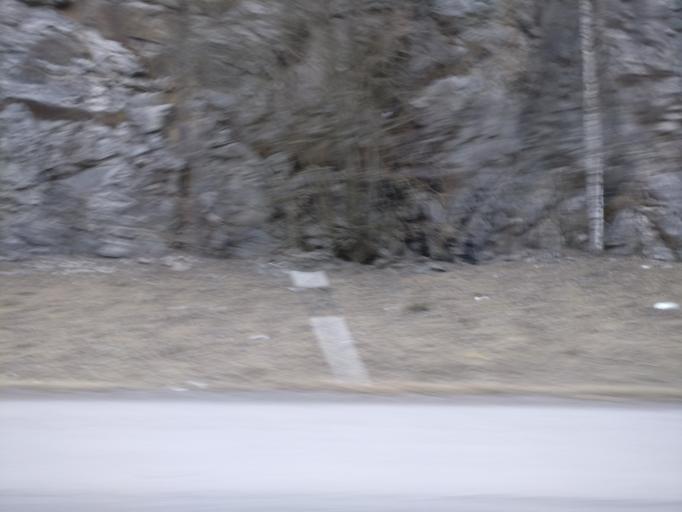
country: FI
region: Uusimaa
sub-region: Helsinki
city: Nurmijaervi
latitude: 60.3879
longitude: 24.8144
